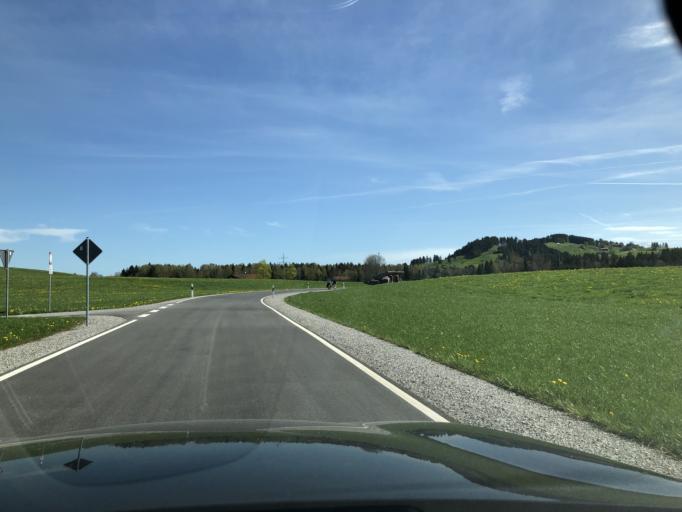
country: DE
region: Bavaria
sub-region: Swabia
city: Seeg
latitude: 47.6457
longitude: 10.6140
